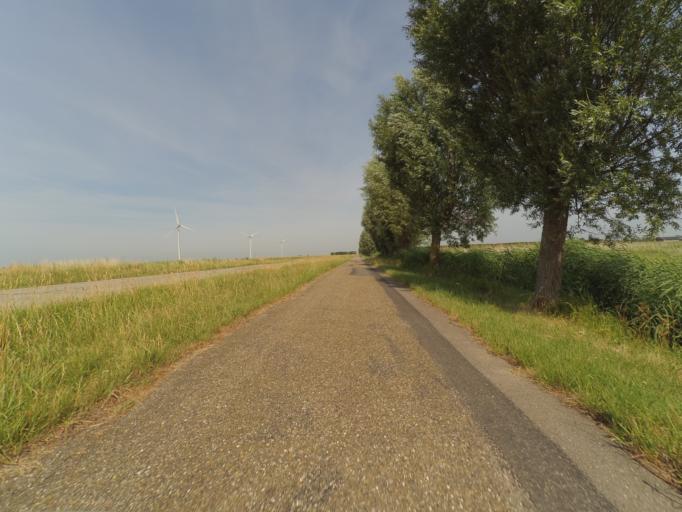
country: NL
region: Zeeland
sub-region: Schouwen-Duiveland
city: Bruinisse
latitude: 51.6344
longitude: 4.1223
